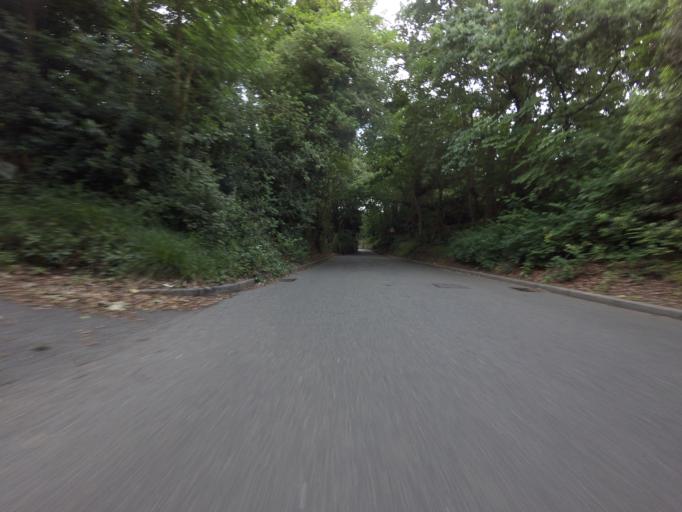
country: GB
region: England
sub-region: Greater London
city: Sidcup
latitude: 51.4243
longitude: 0.1154
